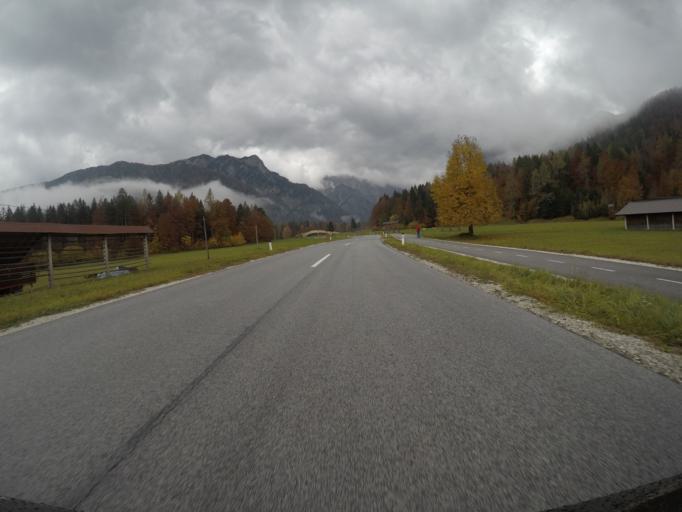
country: AT
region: Carinthia
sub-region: Politischer Bezirk Villach Land
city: Arnoldstein
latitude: 46.4892
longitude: 13.7239
